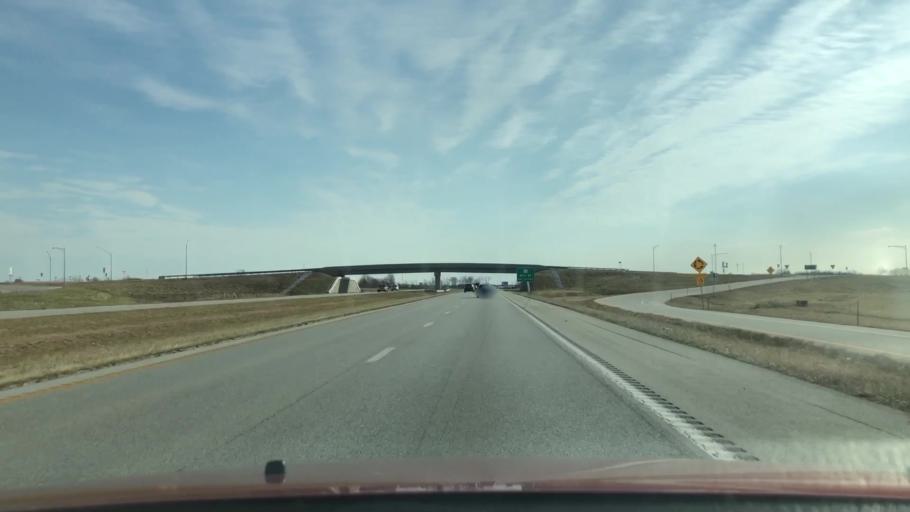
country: US
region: Missouri
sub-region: Webster County
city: Rogersville
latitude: 37.1137
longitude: -93.0756
